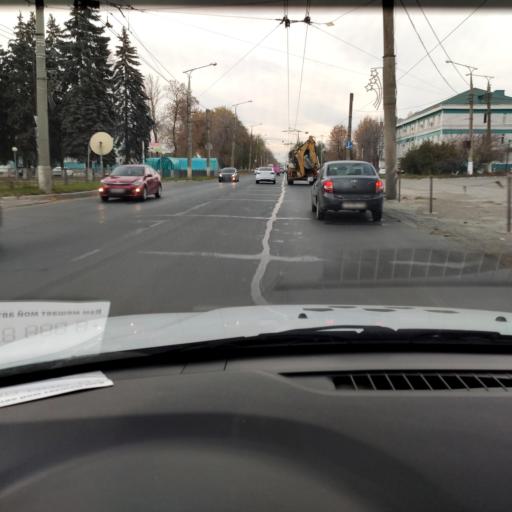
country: RU
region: Samara
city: Tol'yatti
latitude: 53.5418
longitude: 49.4438
